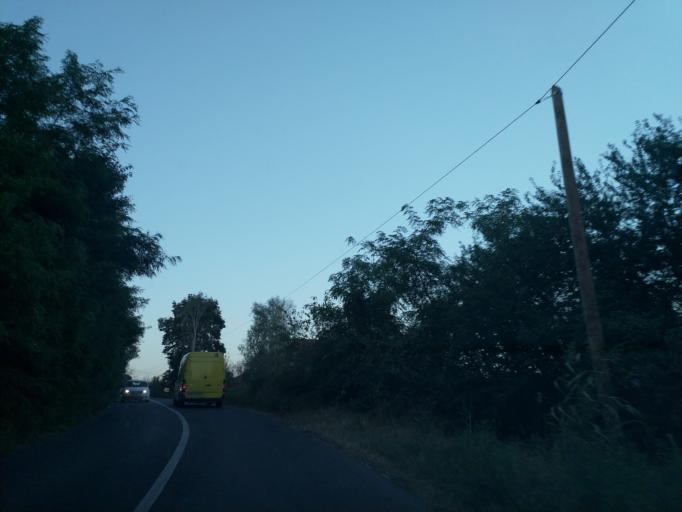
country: RS
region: Central Serbia
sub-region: Rasinski Okrug
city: Krusevac
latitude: 43.6061
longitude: 21.2865
